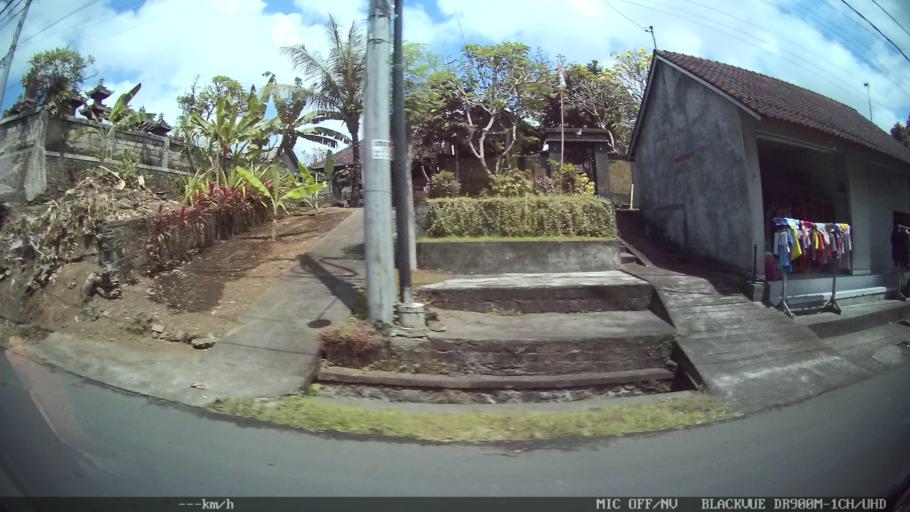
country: ID
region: Bali
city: Banjar Pasekan
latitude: -8.5907
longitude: 115.2860
